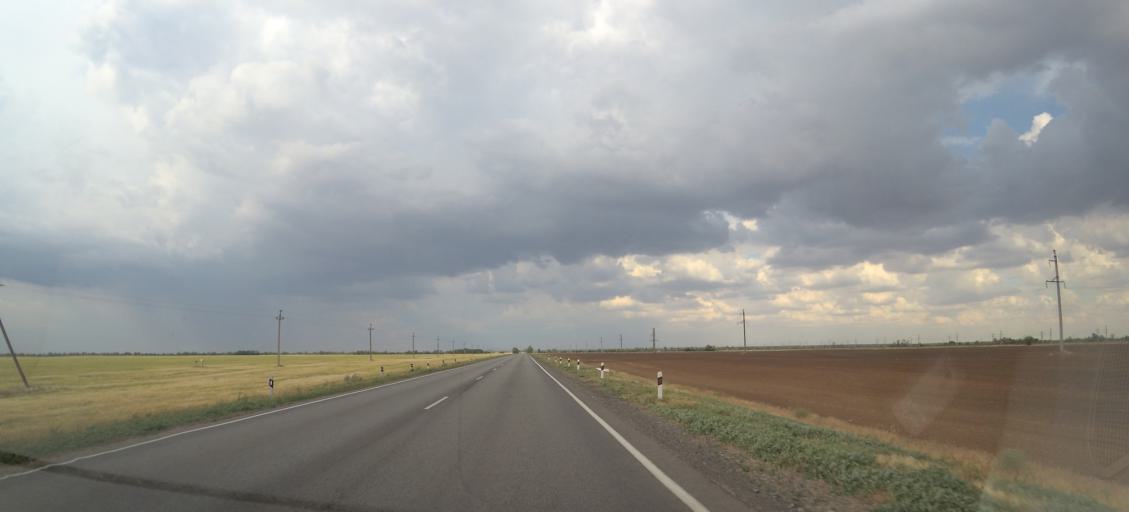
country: RU
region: Rostov
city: Zimovniki
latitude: 47.1213
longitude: 42.3929
